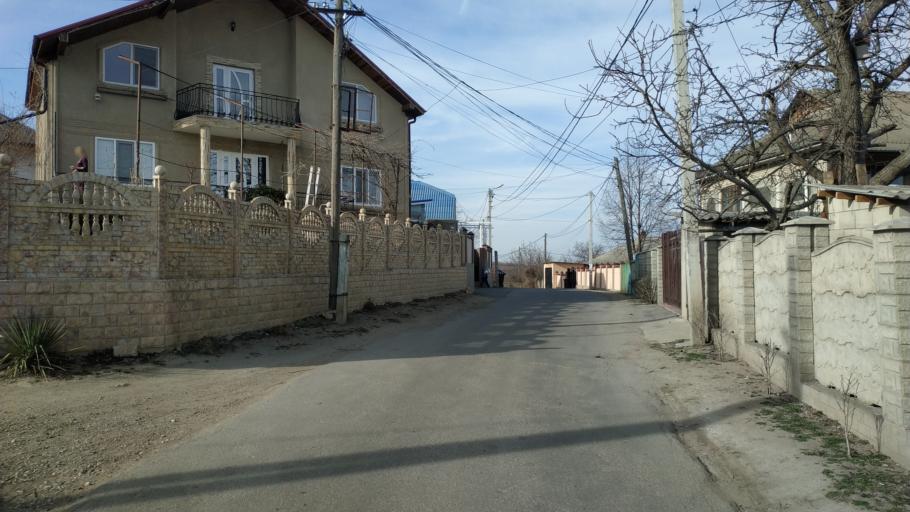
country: MD
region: Chisinau
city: Vatra
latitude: 47.0735
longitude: 28.6718
